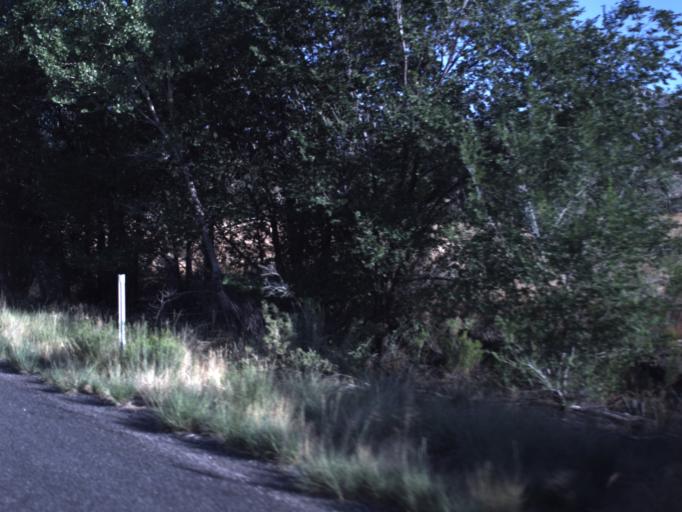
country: US
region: Utah
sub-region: Emery County
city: Huntington
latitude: 39.3531
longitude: -111.0129
